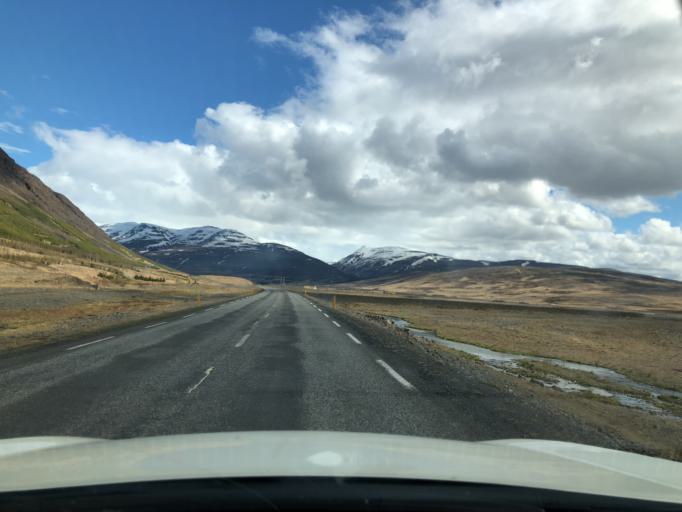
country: IS
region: Northwest
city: Saudarkrokur
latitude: 65.4360
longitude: -19.1772
